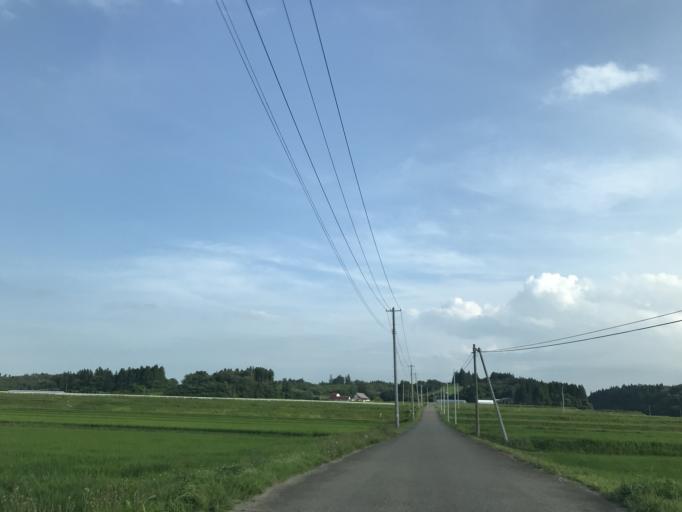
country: JP
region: Iwate
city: Ichinoseki
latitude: 38.8414
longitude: 141.1352
